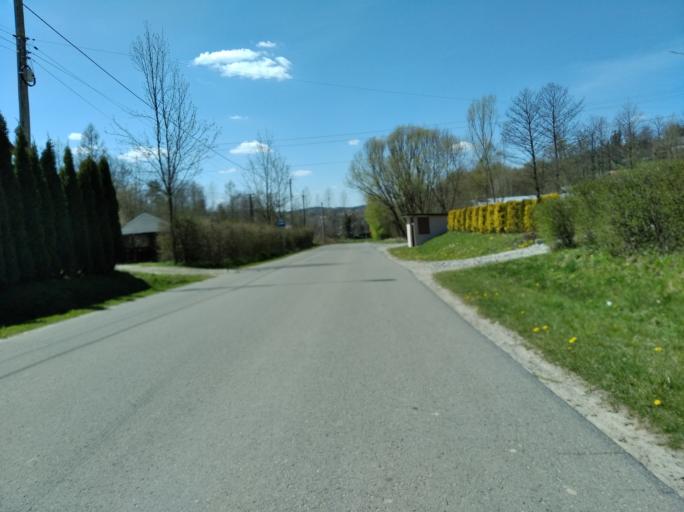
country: PL
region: Subcarpathian Voivodeship
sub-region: Powiat brzozowski
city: Golcowa
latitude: 49.7692
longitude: 22.0382
